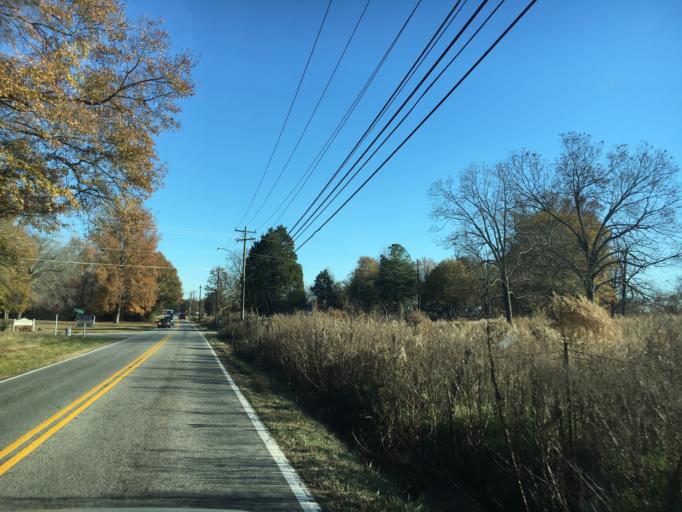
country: US
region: South Carolina
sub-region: Spartanburg County
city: Lyman
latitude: 34.9590
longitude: -82.1319
